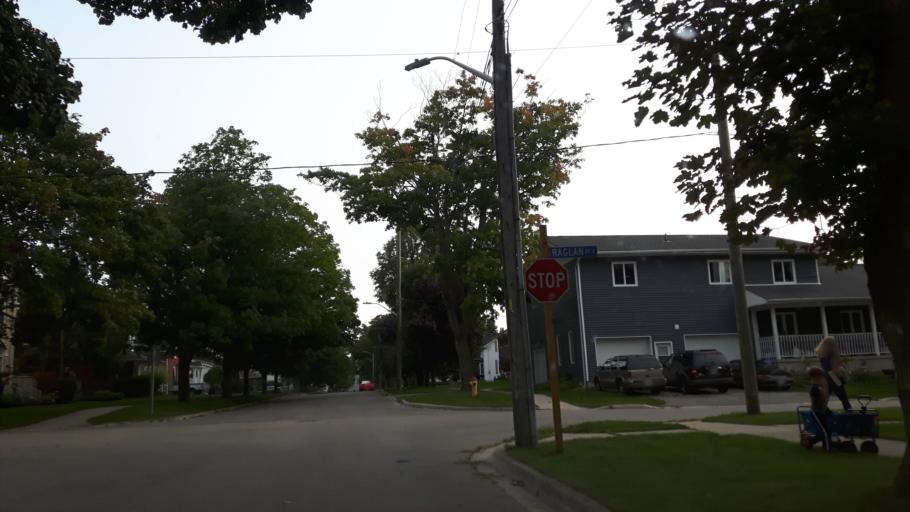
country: CA
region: Ontario
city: Goderich
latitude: 43.7374
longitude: -81.7100
